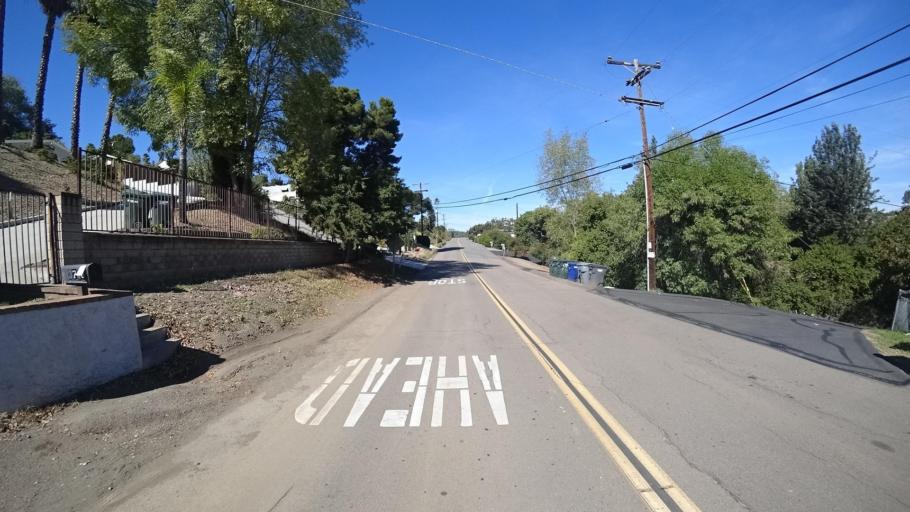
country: US
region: California
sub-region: San Diego County
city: Casa de Oro-Mount Helix
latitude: 32.7468
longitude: -116.9650
